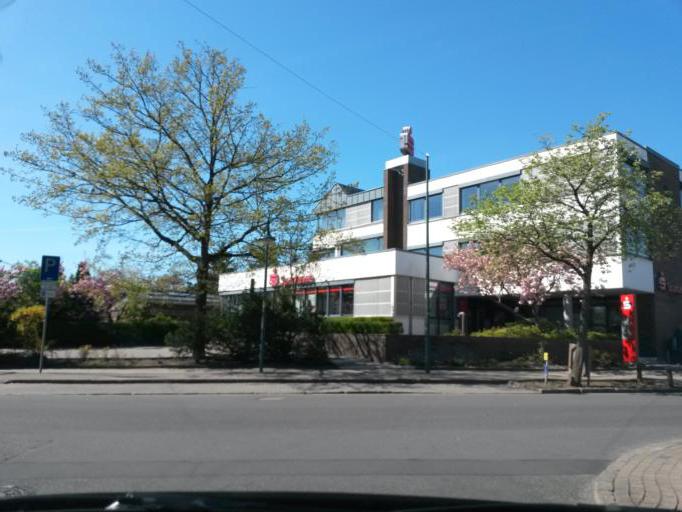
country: DE
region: Schleswig-Holstein
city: Halstenbek
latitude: 53.6348
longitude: 9.8397
